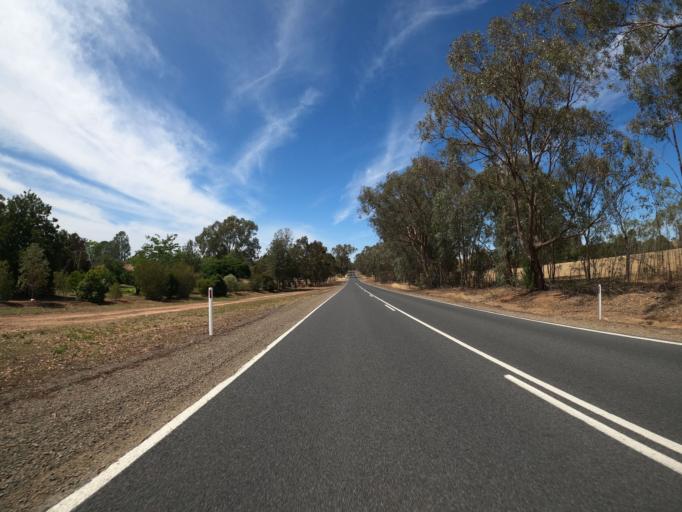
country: AU
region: Victoria
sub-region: Benalla
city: Benalla
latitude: -36.3844
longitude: 145.9787
